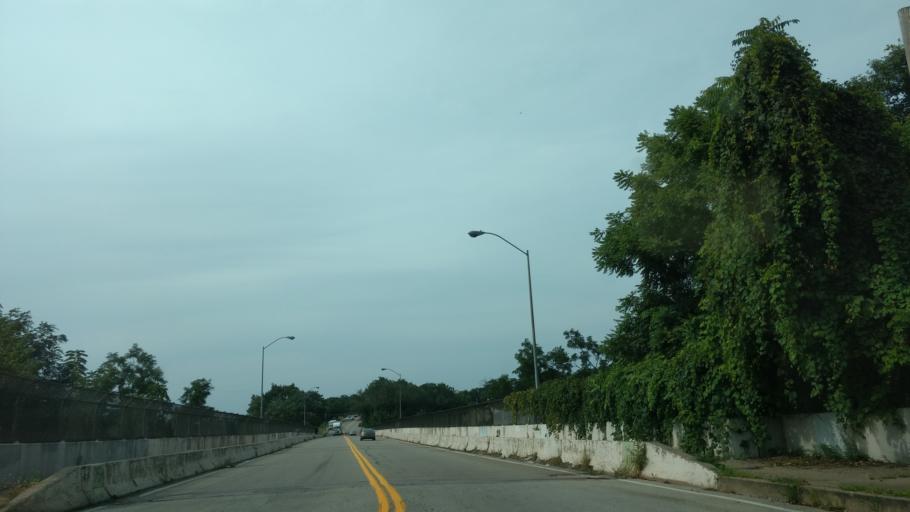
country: US
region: Pennsylvania
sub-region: Allegheny County
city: Bellevue
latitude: 40.4707
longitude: -80.0362
